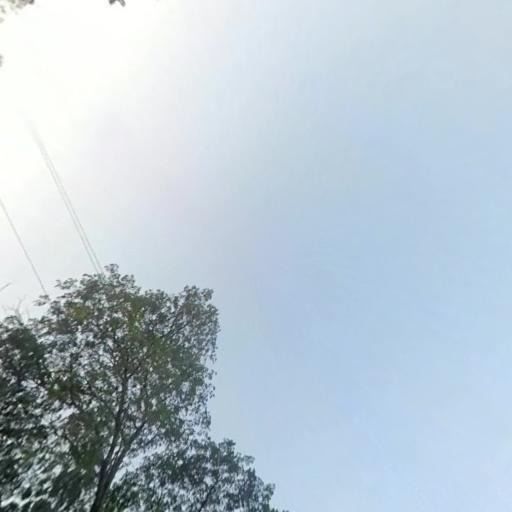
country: IN
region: Telangana
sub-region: Nalgonda
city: Suriapet
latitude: 17.1053
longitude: 79.5285
